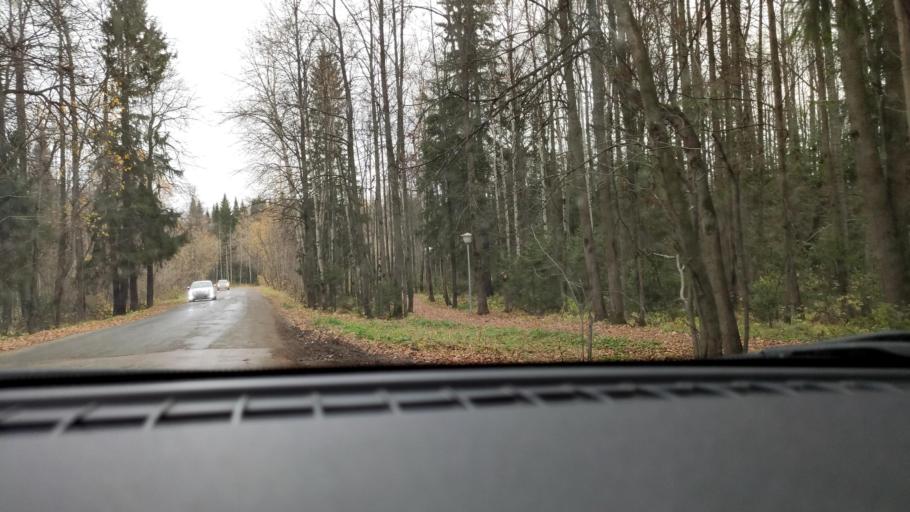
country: RU
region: Perm
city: Froly
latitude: 57.9538
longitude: 56.3010
